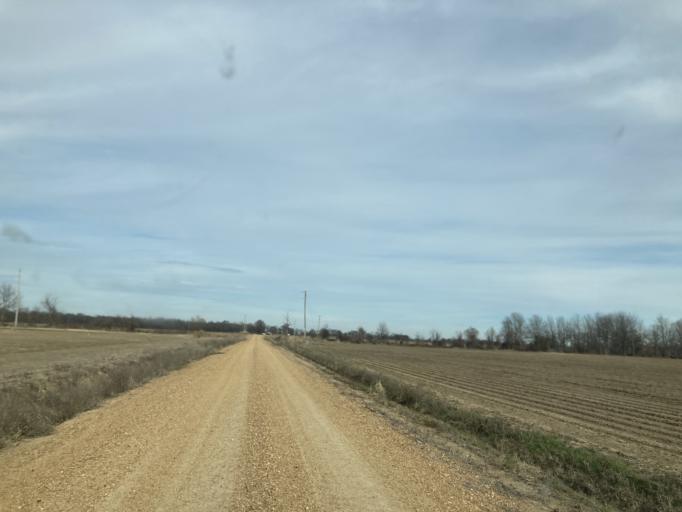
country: US
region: Mississippi
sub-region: Humphreys County
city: Belzoni
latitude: 33.0575
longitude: -90.6577
